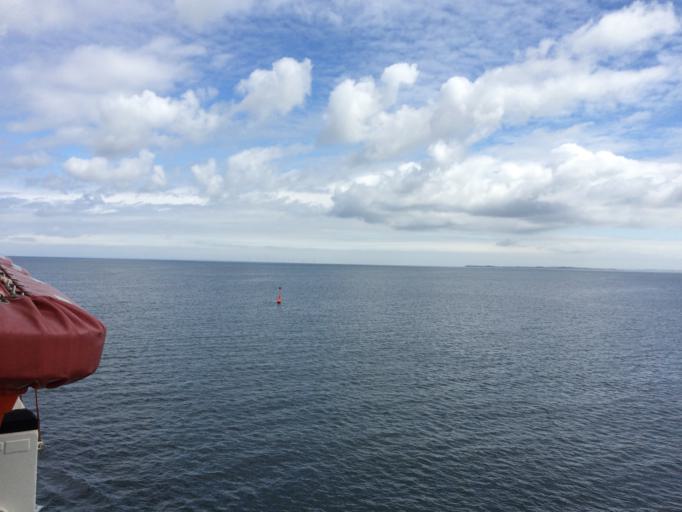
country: DK
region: Central Jutland
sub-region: Odder Kommune
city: Odder
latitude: 55.9164
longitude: 10.2688
